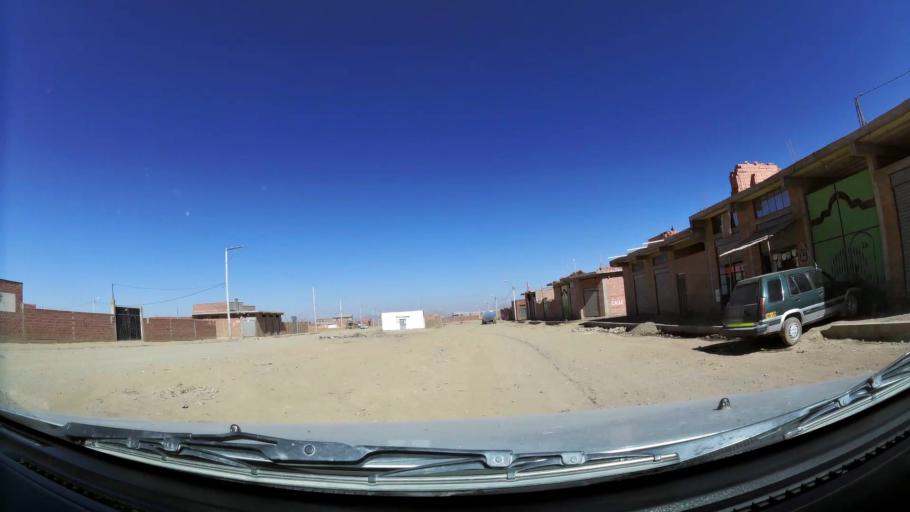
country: BO
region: La Paz
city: La Paz
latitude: -16.6253
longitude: -68.1937
